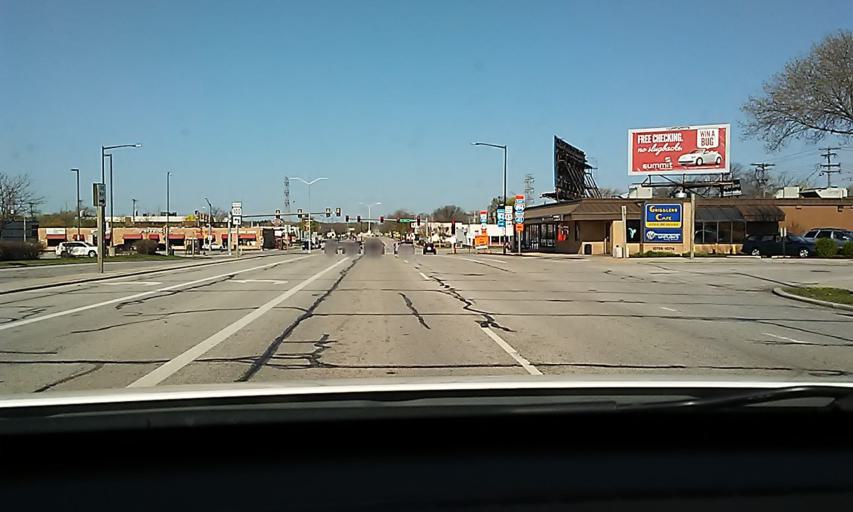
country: US
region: Wisconsin
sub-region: Milwaukee County
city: West Allis
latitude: 43.0164
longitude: -88.0453
